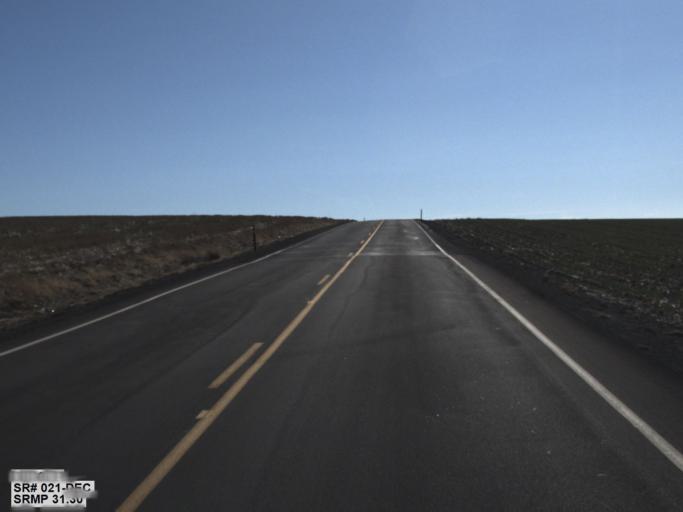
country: US
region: Washington
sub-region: Adams County
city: Ritzville
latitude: 47.0036
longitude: -118.6637
